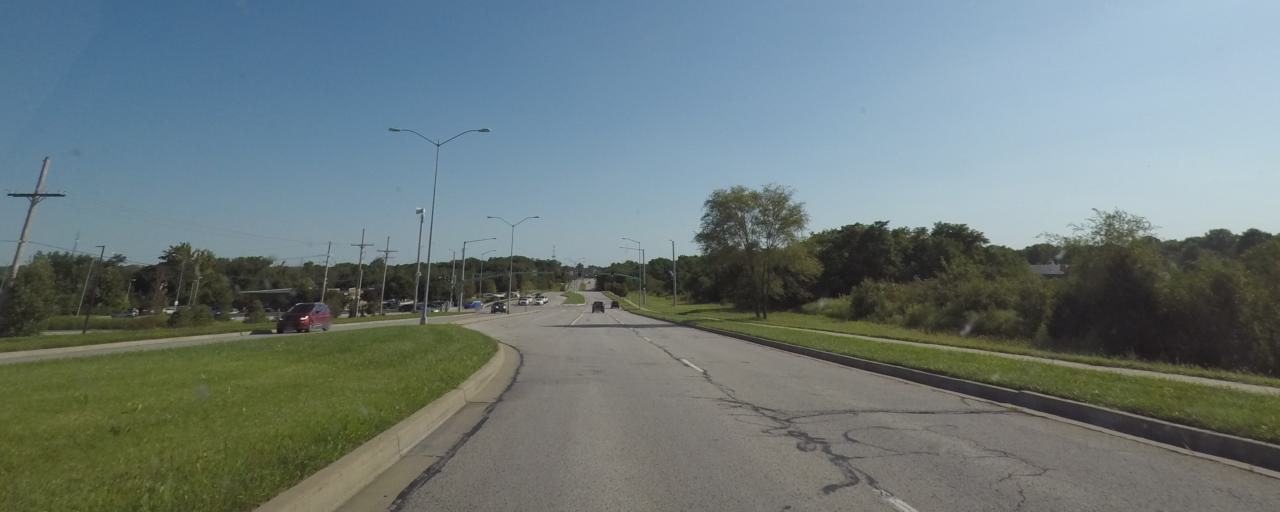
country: US
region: Missouri
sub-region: Clay County
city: Gladstone
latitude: 39.2543
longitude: -94.6009
